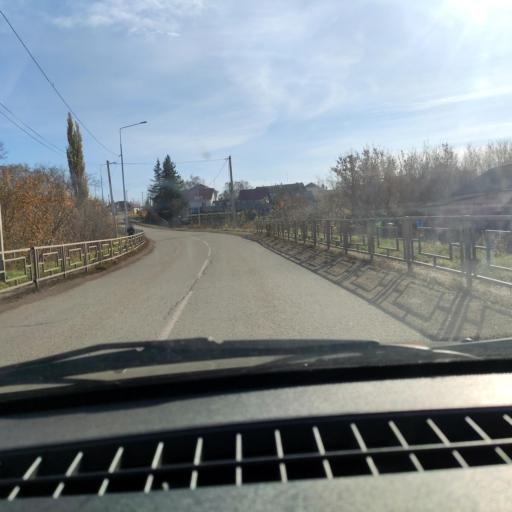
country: RU
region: Bashkortostan
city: Avdon
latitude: 54.5001
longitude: 55.8828
